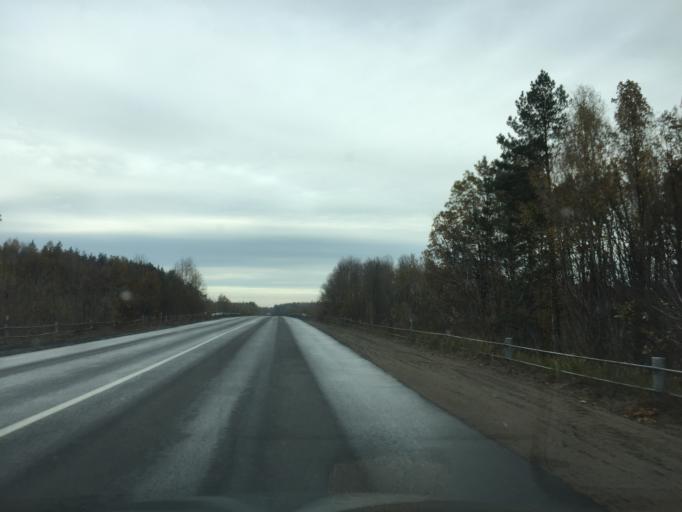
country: BY
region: Gomel
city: Gomel
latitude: 52.4157
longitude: 30.8287
